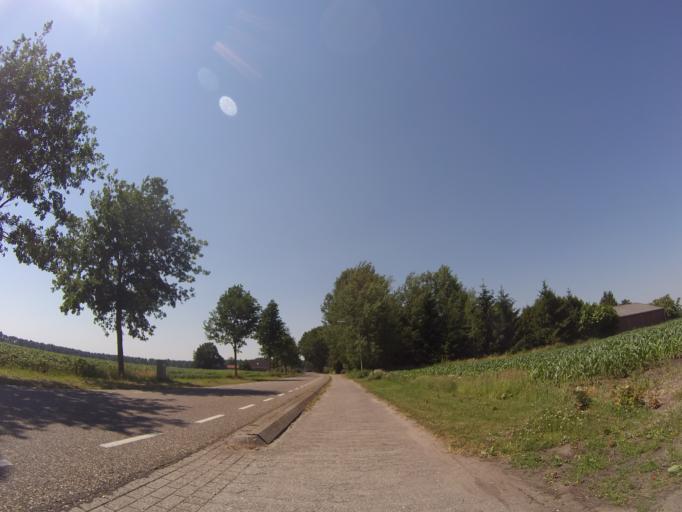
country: NL
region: Drenthe
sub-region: Gemeente Coevorden
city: Sleen
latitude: 52.8099
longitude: 6.8113
